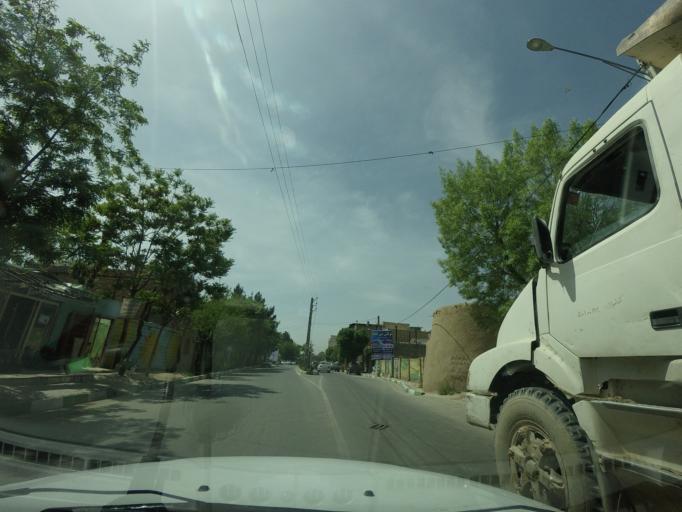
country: IR
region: Tehran
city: Eslamshahr
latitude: 35.6288
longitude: 51.2517
